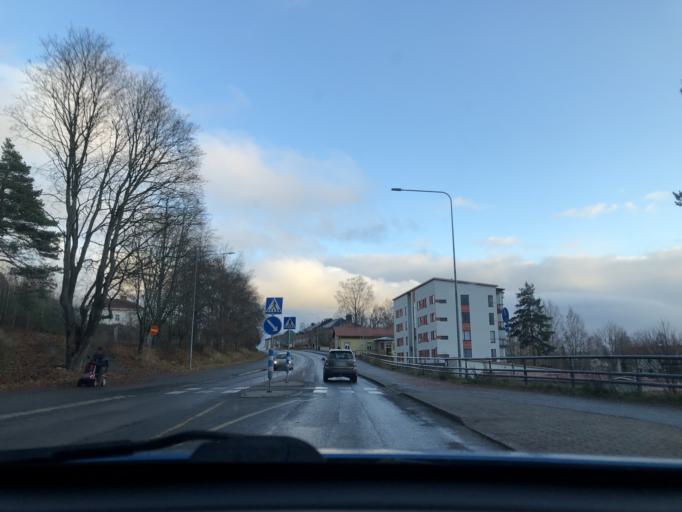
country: FI
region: Pirkanmaa
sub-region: Tampere
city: Kangasala
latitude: 61.4645
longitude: 24.0589
